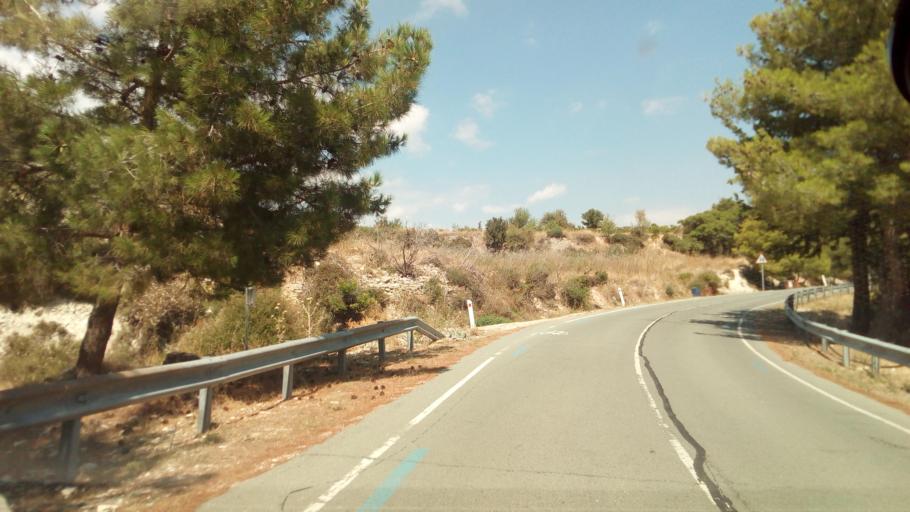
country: CY
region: Limassol
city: Pachna
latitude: 34.8331
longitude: 32.8512
